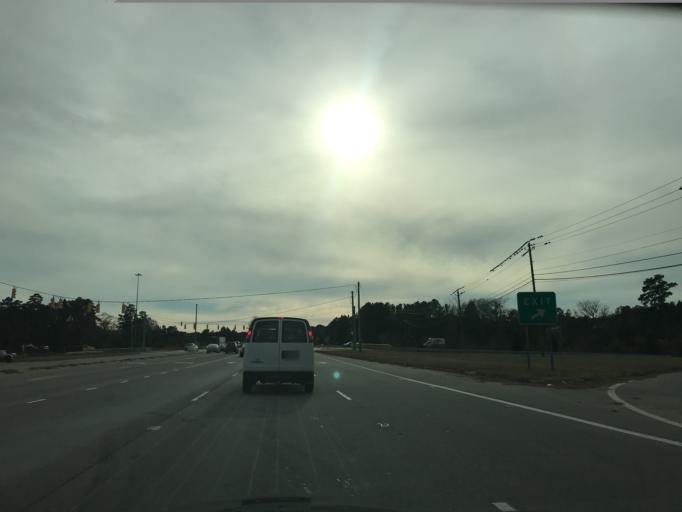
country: US
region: North Carolina
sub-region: Wake County
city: Knightdale
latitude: 35.8632
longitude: -78.5481
